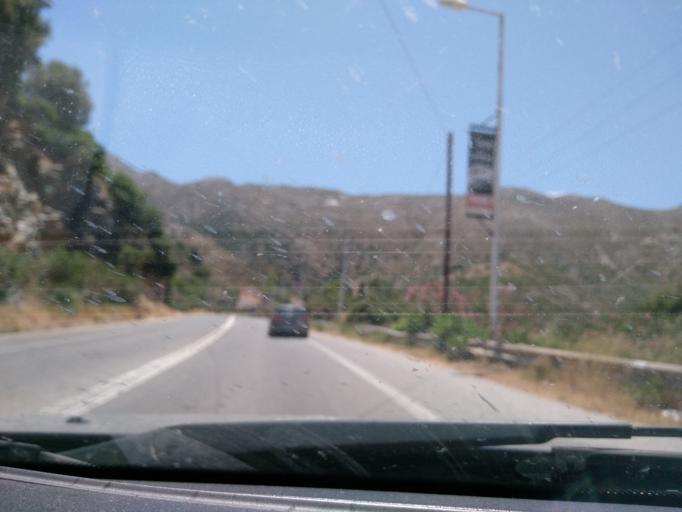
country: GR
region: Crete
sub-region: Nomos Rethymnis
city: Anogeia
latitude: 35.3863
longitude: 24.9191
